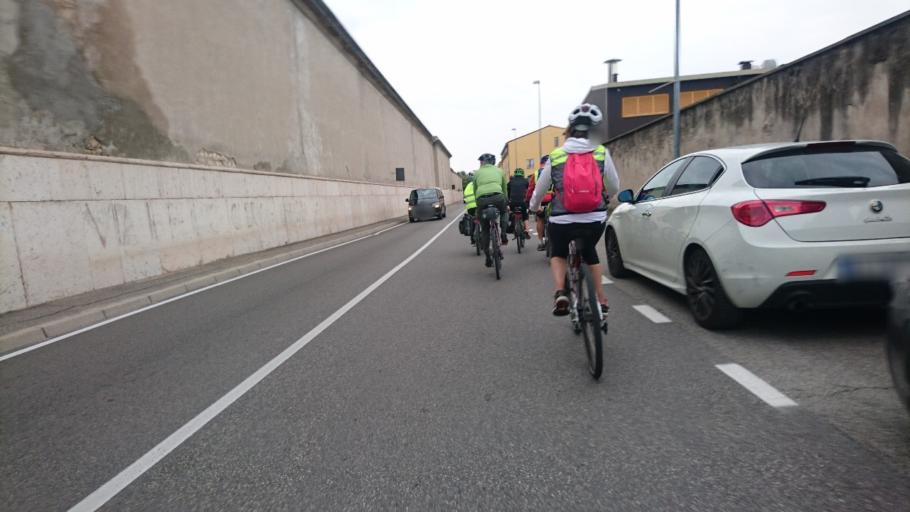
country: IT
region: Veneto
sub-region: Provincia di Verona
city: Verona
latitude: 45.4316
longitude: 11.0026
